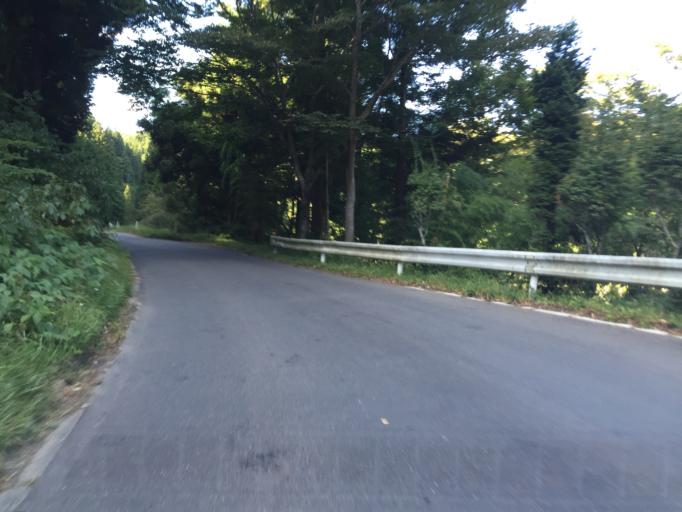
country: JP
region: Miyagi
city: Marumori
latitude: 37.8462
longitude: 140.7425
